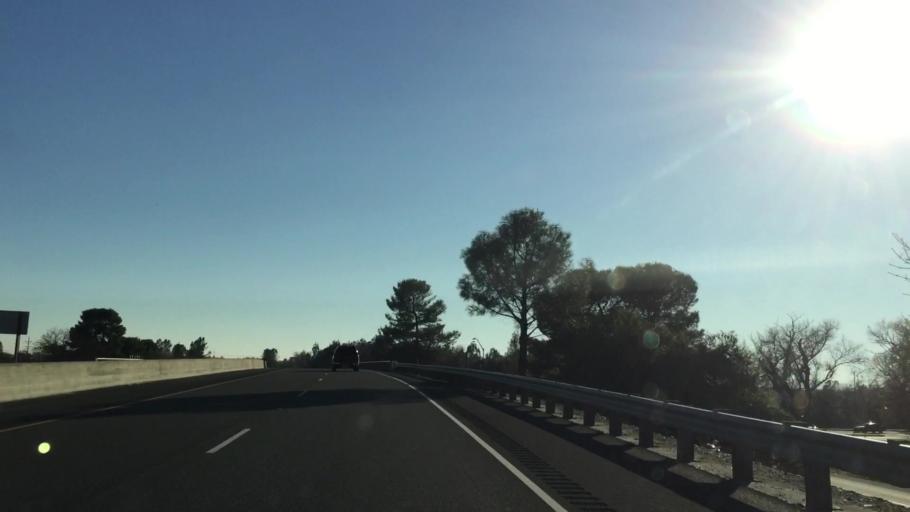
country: US
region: California
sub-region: Butte County
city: Thermalito
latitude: 39.4989
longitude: -121.5753
